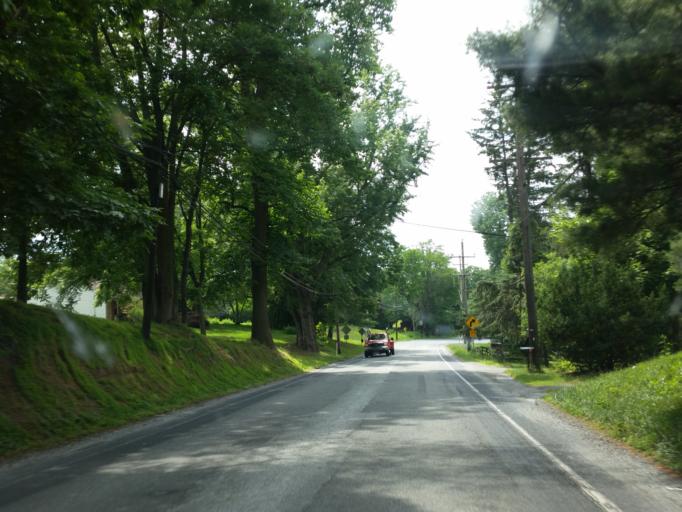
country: US
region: Pennsylvania
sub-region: Chester County
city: West Grove
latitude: 39.7607
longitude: -75.8429
